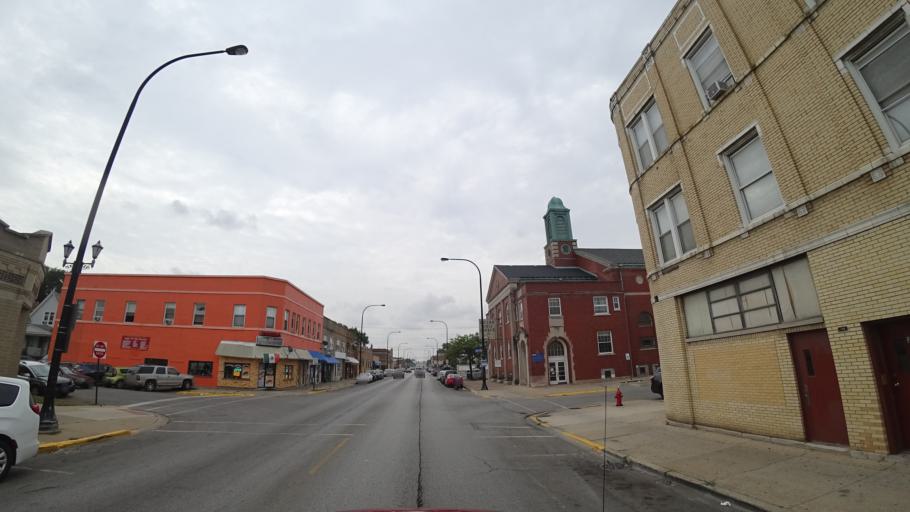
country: US
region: Illinois
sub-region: Cook County
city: Cicero
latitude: 41.8505
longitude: -87.7541
